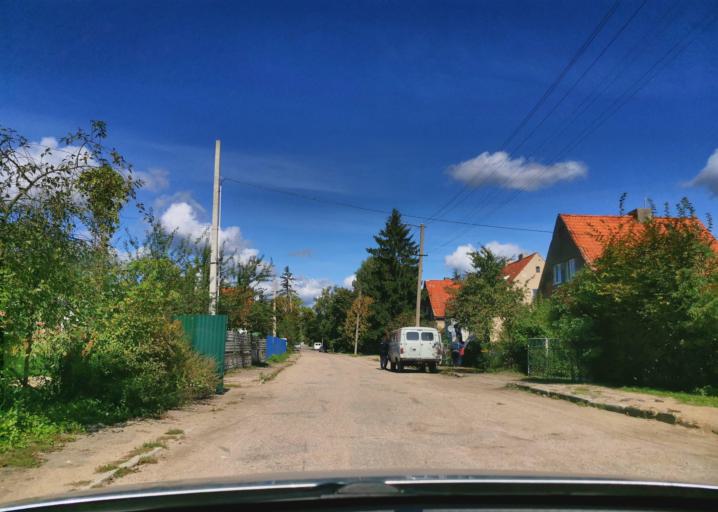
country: RU
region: Kaliningrad
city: Chernyakhovsk
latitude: 54.6345
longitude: 21.8408
